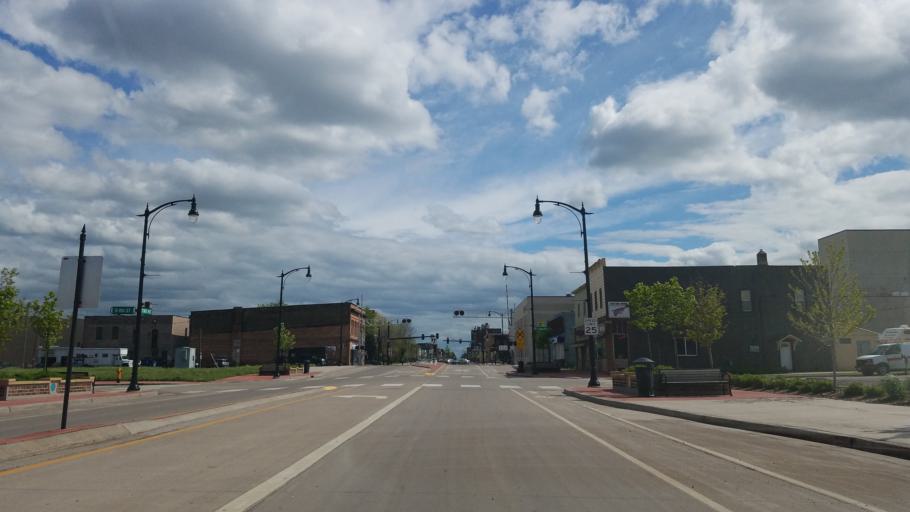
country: US
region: Wisconsin
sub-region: Douglas County
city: Superior
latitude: 46.7296
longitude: -92.1040
